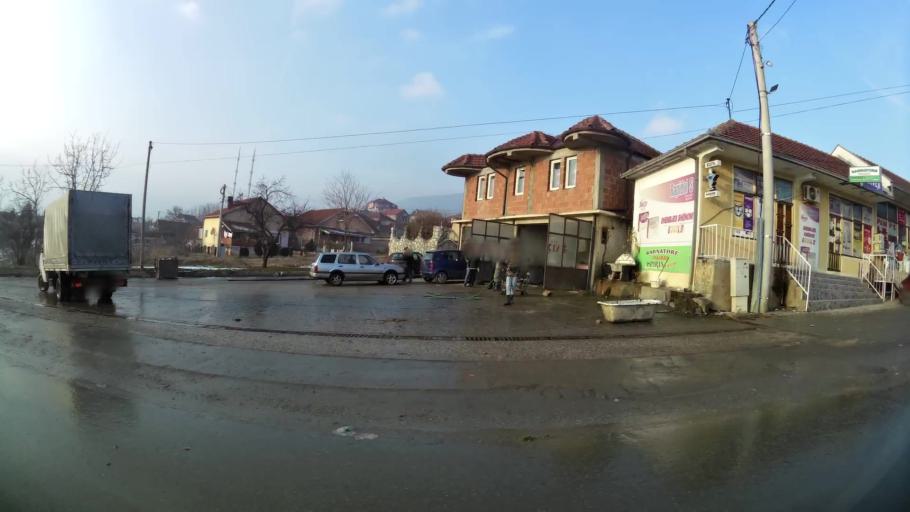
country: MK
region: Aracinovo
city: Arachinovo
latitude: 42.0265
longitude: 21.5620
